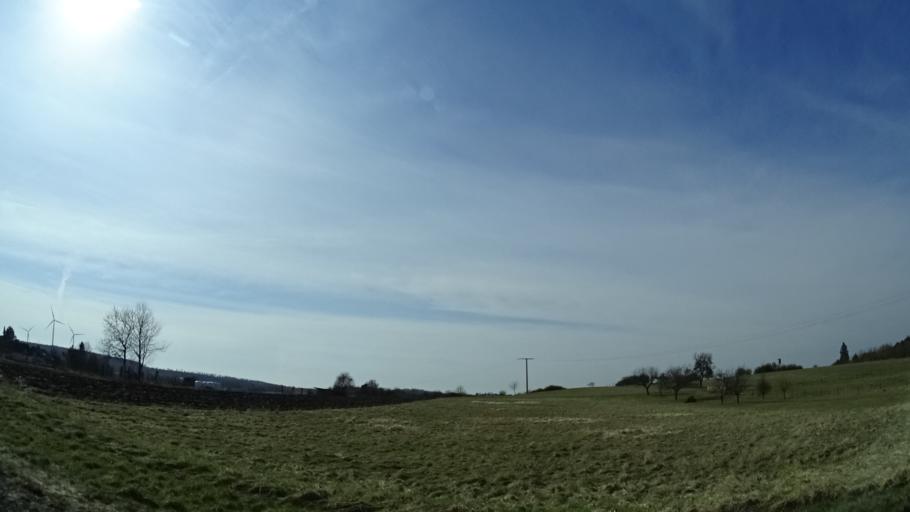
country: DE
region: Hesse
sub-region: Regierungsbezirk Giessen
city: Grunberg
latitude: 50.6143
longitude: 8.9795
